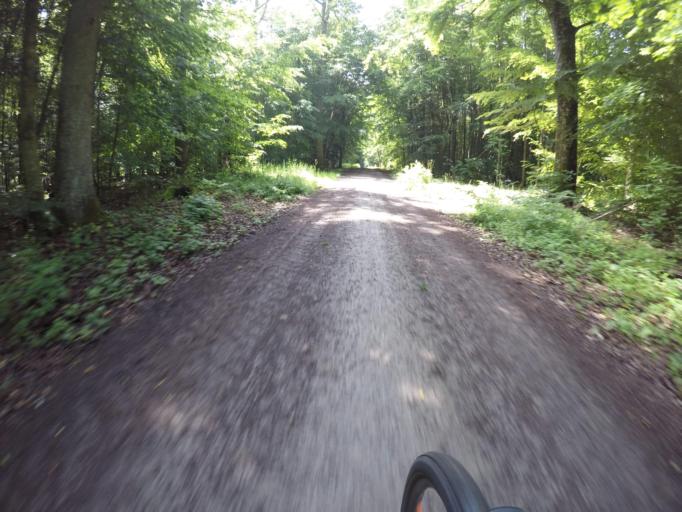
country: DE
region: Baden-Wuerttemberg
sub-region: Regierungsbezirk Stuttgart
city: Nufringen
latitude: 48.6350
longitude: 8.8590
